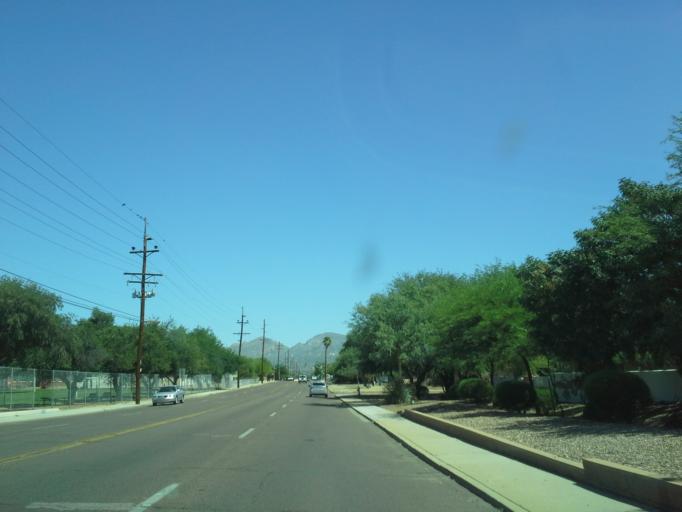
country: US
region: Arizona
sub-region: Pima County
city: Tucson
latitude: 32.2407
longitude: -110.9267
